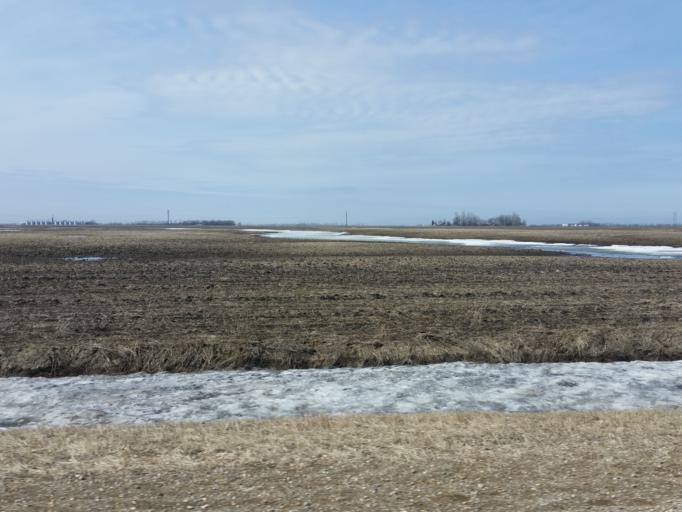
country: US
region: North Dakota
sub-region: Walsh County
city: Grafton
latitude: 48.2995
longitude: -97.2549
